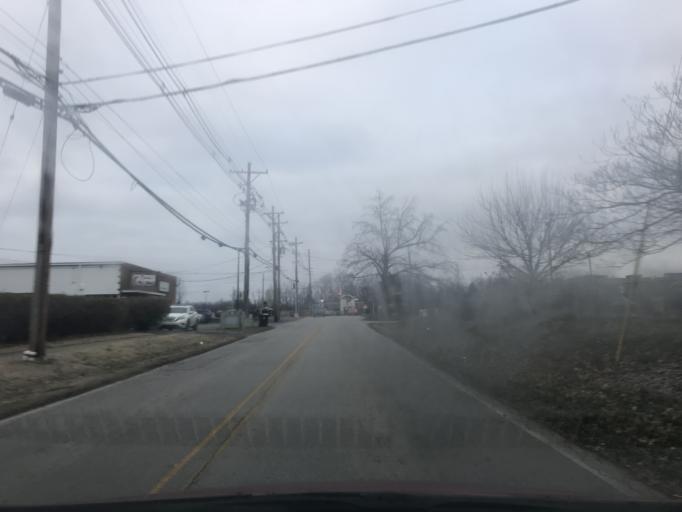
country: US
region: Kentucky
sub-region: Jefferson County
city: Audubon Park
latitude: 38.2114
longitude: -85.7222
